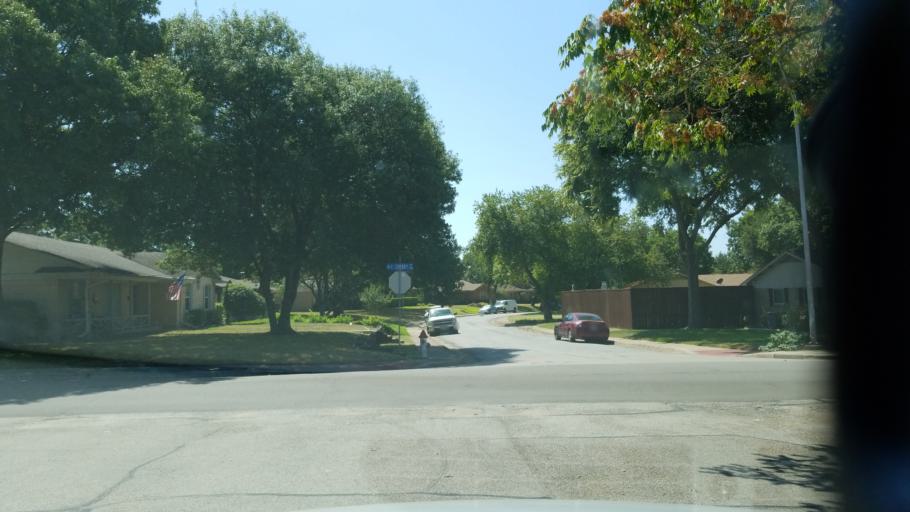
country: US
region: Texas
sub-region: Dallas County
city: Duncanville
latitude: 32.6533
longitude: -96.8986
